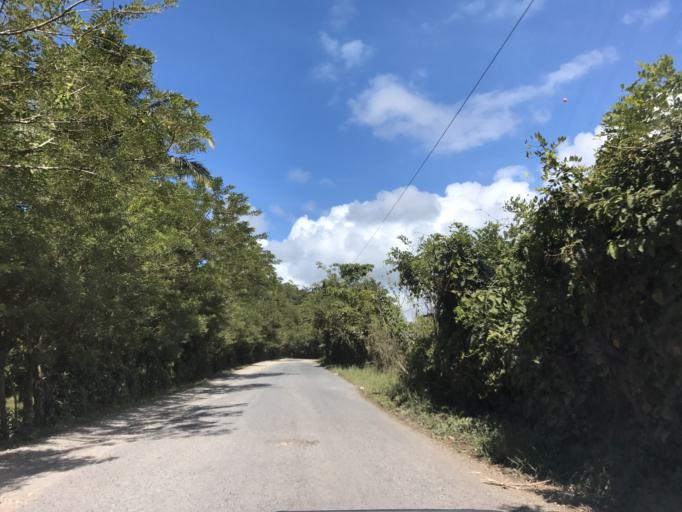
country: GT
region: Izabal
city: Morales
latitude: 15.6461
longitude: -89.0186
